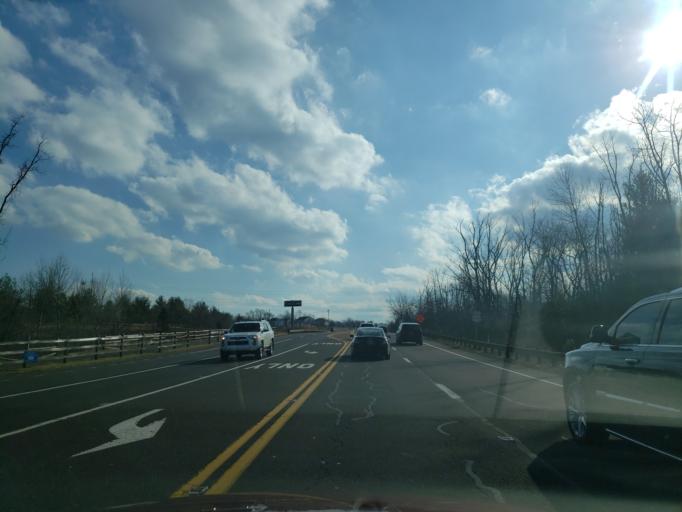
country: US
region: Pennsylvania
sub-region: Montgomery County
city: Montgomeryville
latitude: 40.2259
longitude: -75.2422
